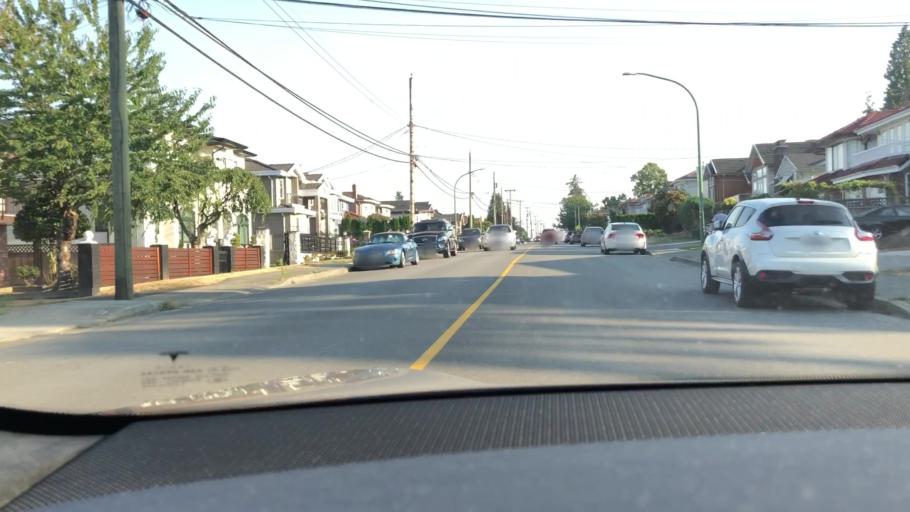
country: CA
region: British Columbia
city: Burnaby
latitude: 49.2240
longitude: -122.9720
